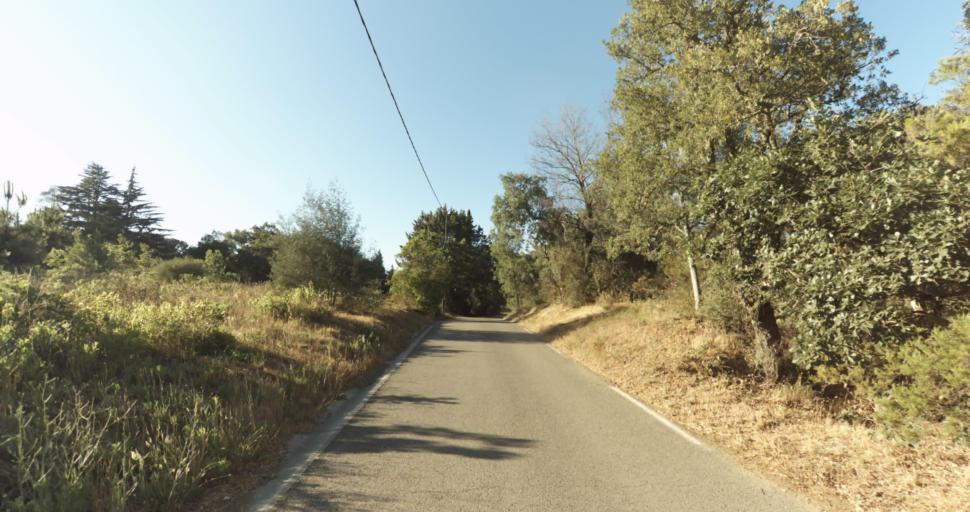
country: FR
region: Provence-Alpes-Cote d'Azur
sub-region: Departement du Var
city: Gassin
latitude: 43.2313
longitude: 6.5941
